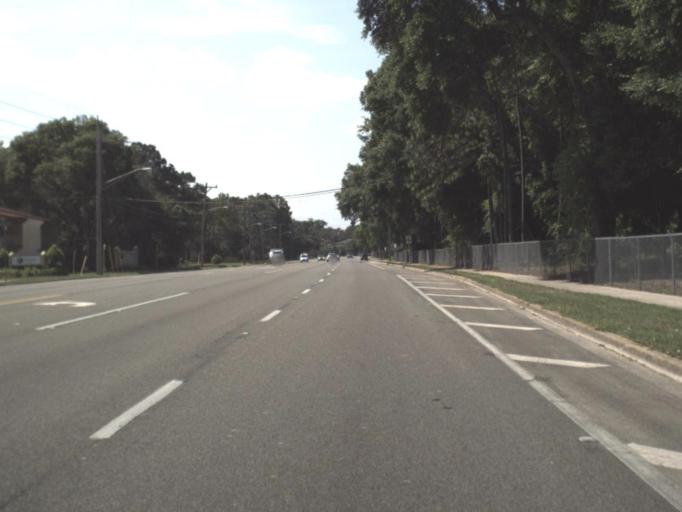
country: US
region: Florida
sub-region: Duval County
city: Jacksonville
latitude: 30.3568
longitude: -81.6044
